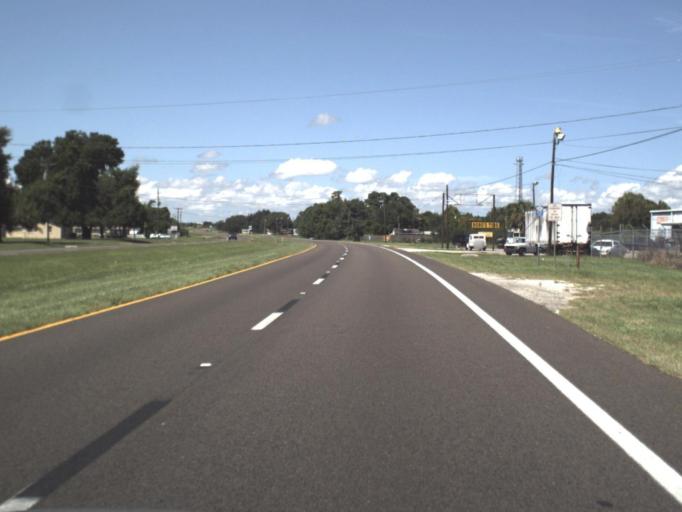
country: US
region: Florida
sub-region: Polk County
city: Haines City
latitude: 28.1081
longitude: -81.6683
